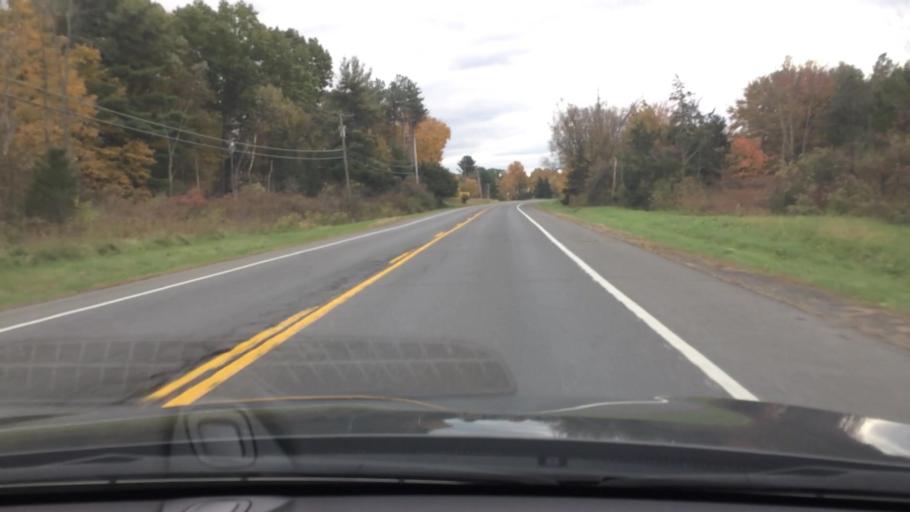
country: US
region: New York
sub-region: Columbia County
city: Oakdale
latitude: 42.1615
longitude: -73.7480
